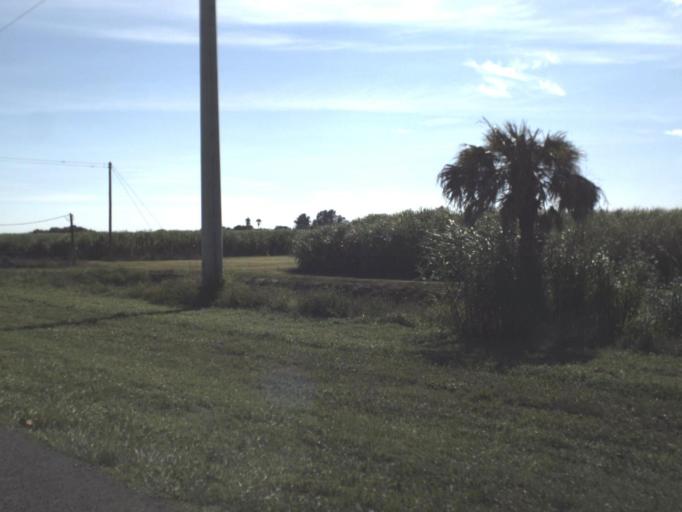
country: US
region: Florida
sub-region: Glades County
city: Moore Haven
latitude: 26.8218
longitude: -81.0826
